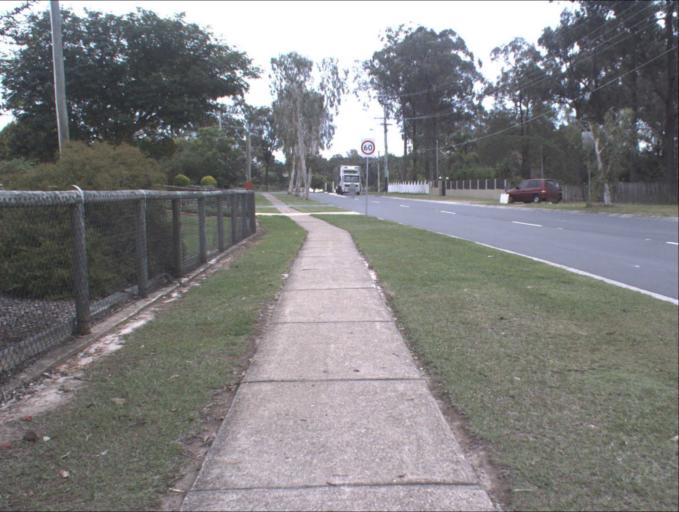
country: AU
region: Queensland
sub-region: Brisbane
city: Forest Lake
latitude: -27.6624
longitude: 153.0080
